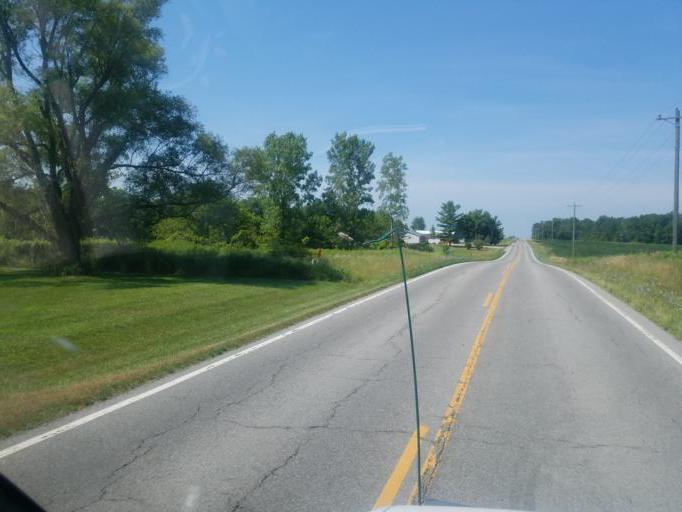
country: US
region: Ohio
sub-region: Union County
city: Marysville
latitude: 40.2106
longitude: -83.4422
